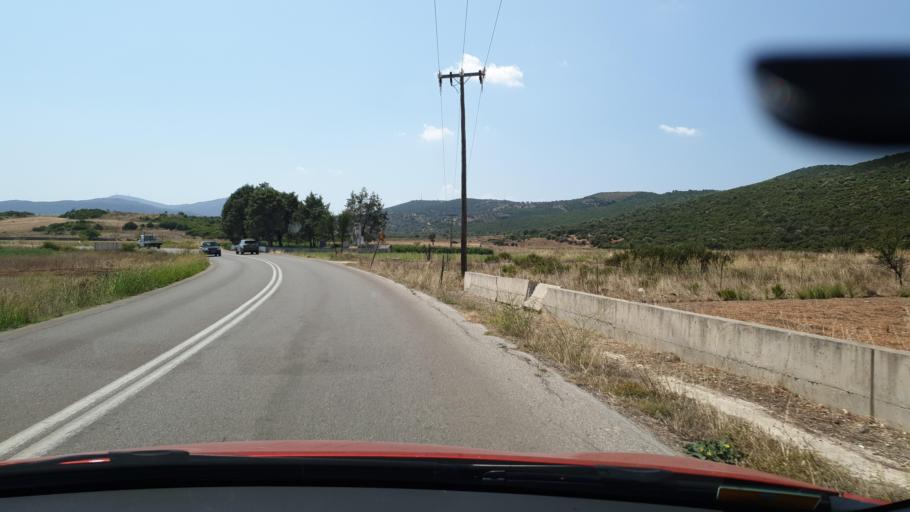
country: GR
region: Central Greece
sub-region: Nomos Evvoias
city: Aliveri
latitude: 38.4260
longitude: 24.1141
